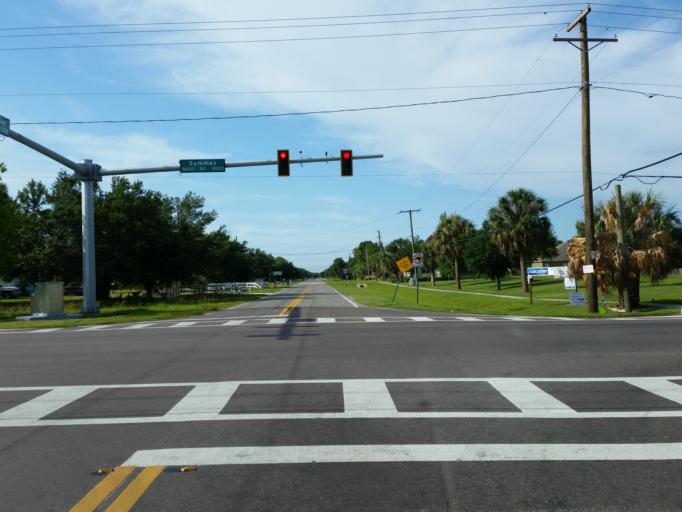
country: US
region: Florida
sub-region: Hillsborough County
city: Gibsonton
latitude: 27.8352
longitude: -82.3528
